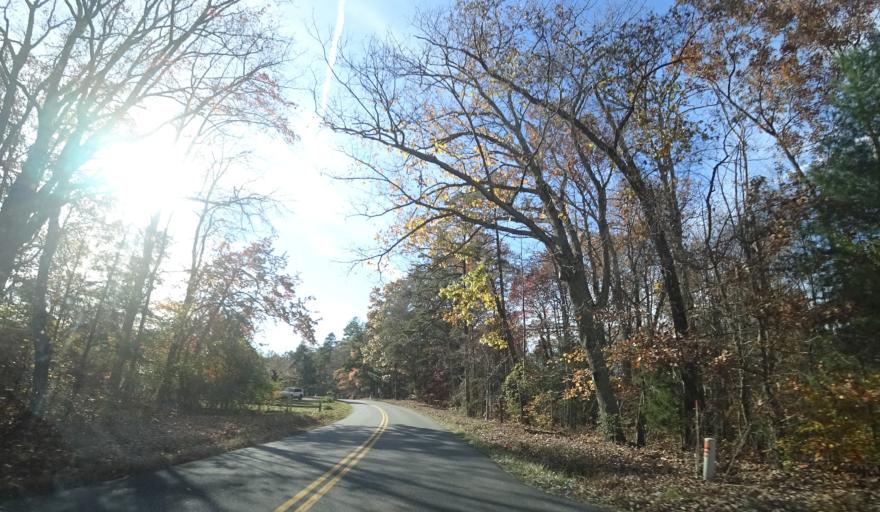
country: US
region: Virginia
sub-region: Greene County
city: Stanardsville
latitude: 38.2832
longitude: -78.3991
